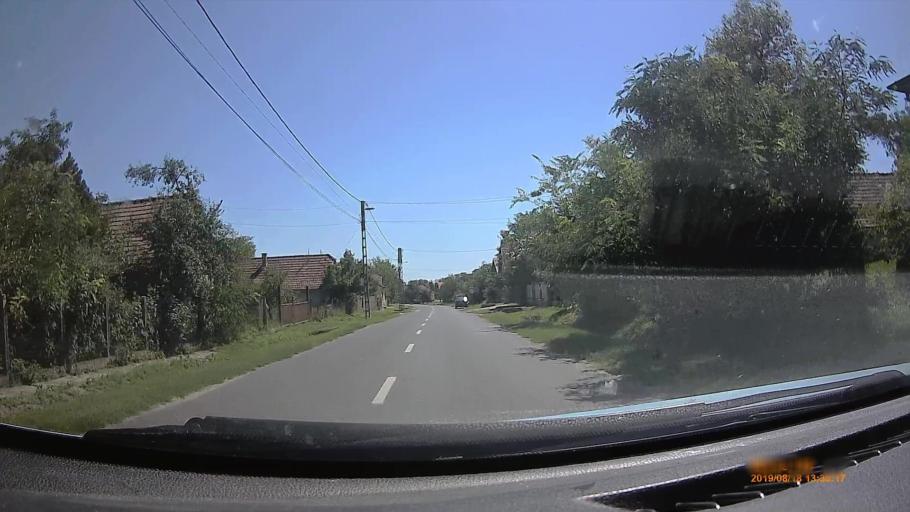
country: HU
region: Fejer
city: Cece
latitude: 46.7827
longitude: 18.5919
